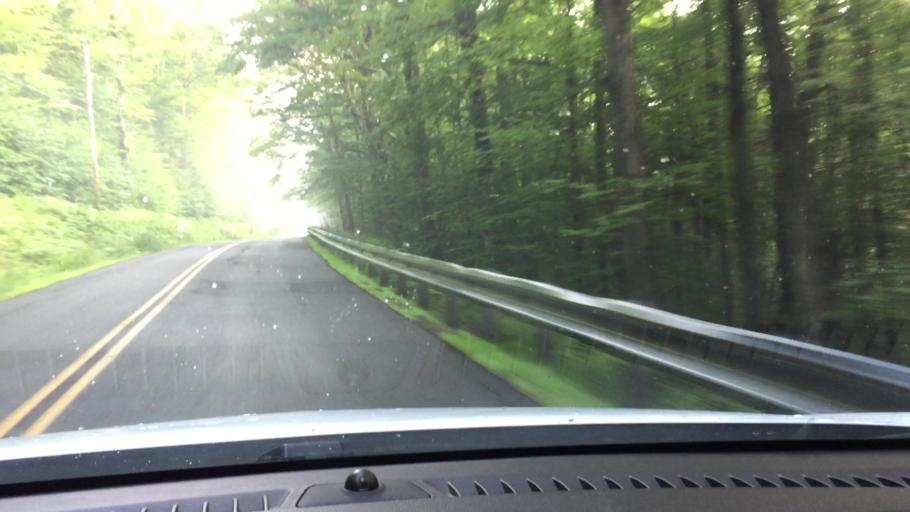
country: US
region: Massachusetts
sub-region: Berkshire County
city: Becket
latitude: 42.4114
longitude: -72.9807
